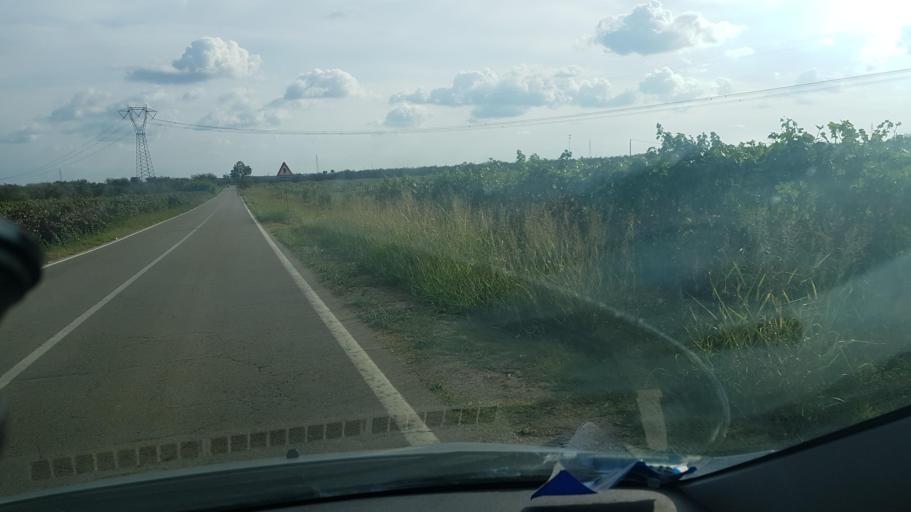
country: IT
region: Apulia
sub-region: Provincia di Brindisi
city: Cellino San Marco
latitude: 40.4557
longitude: 17.9549
